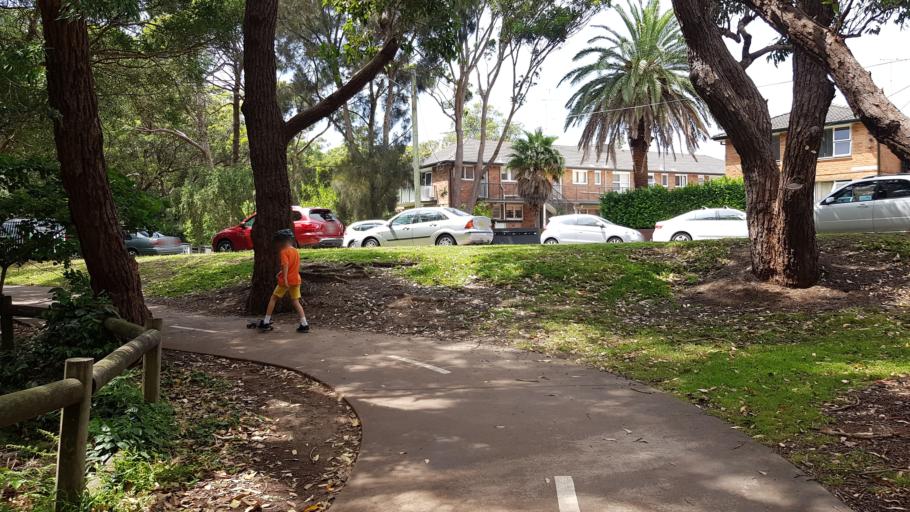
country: AU
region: New South Wales
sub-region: Warringah
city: Dee Why
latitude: -33.7496
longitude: 151.2919
